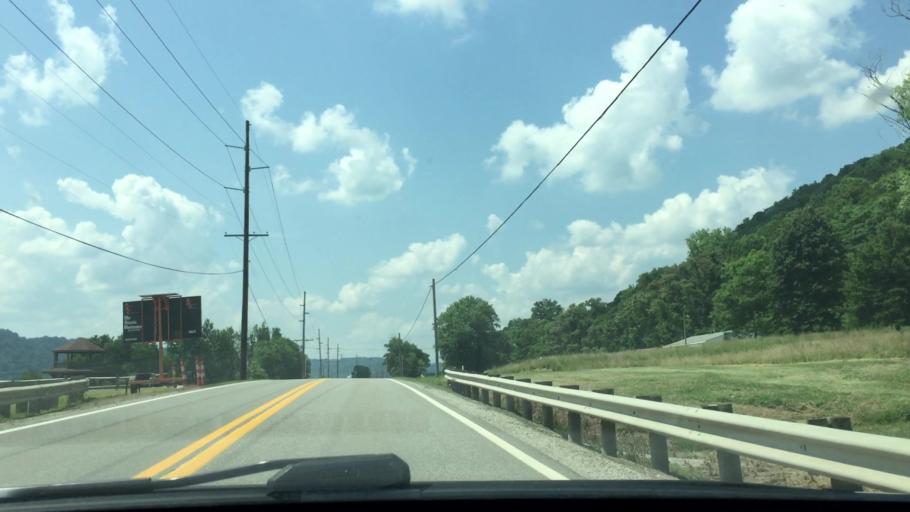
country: US
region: West Virginia
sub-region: Wetzel County
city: New Martinsville
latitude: 39.7357
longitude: -80.8377
